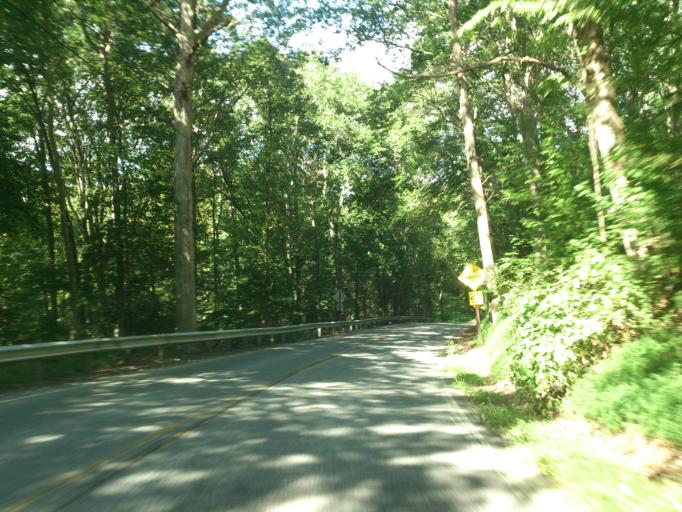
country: US
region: Pennsylvania
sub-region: York County
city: Susquehanna Trails
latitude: 39.8056
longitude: -76.4769
